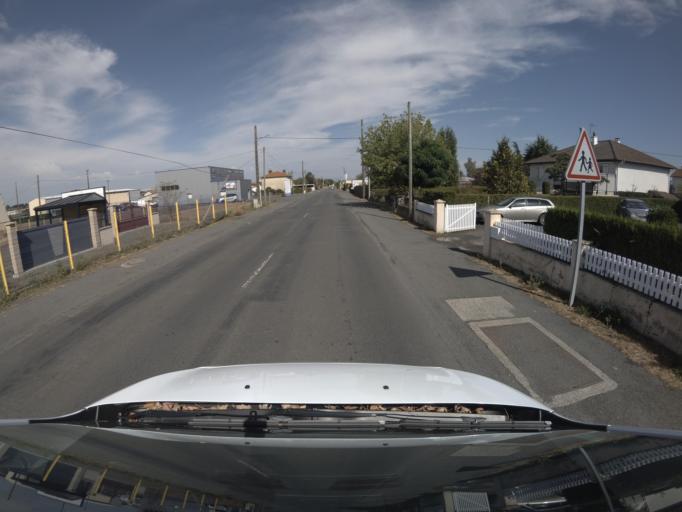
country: FR
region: Poitou-Charentes
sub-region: Departement des Deux-Sevres
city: Argenton-les-Vallees
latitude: 46.9844
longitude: -0.4608
